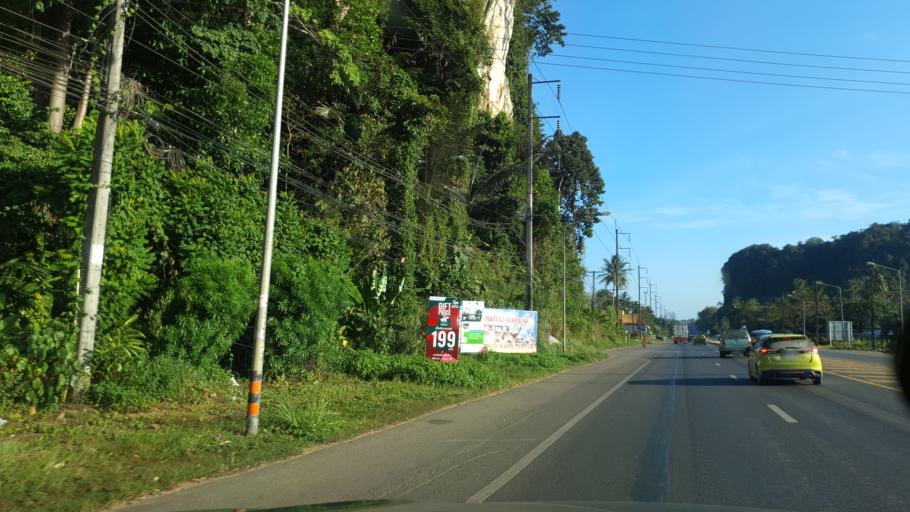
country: TH
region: Krabi
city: Krabi
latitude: 8.1218
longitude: 98.8705
